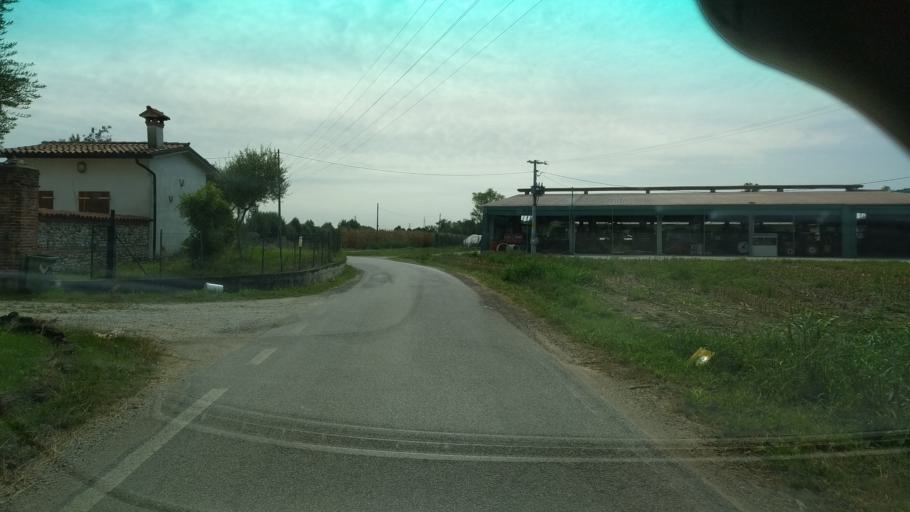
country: IT
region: Veneto
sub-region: Provincia di Vicenza
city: Sandrigo
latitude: 45.6409
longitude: 11.5927
